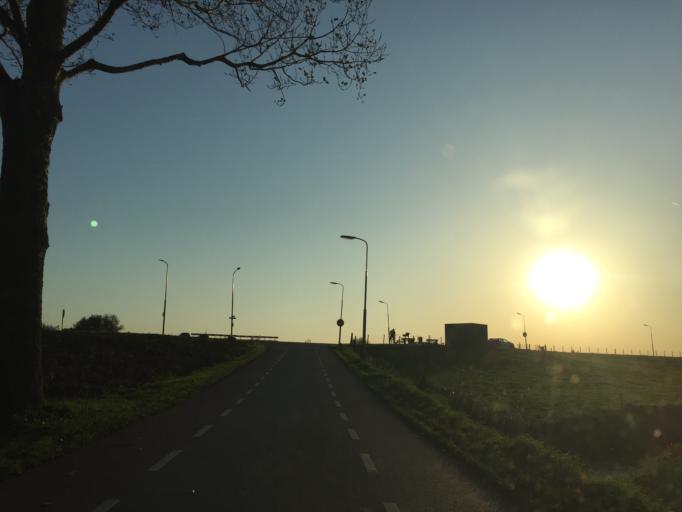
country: NL
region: South Holland
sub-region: Gemeente Kaag en Braassem
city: Oude Wetering
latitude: 52.2155
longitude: 4.6036
